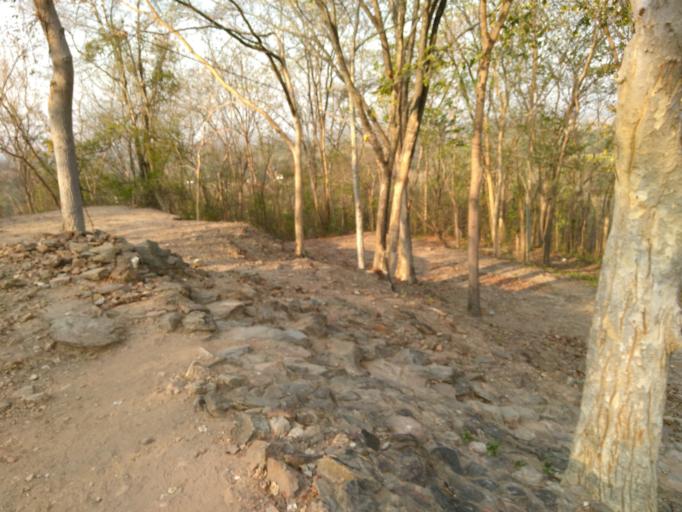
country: TH
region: Sukhothai
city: Ban Na
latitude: 17.0233
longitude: 99.6752
